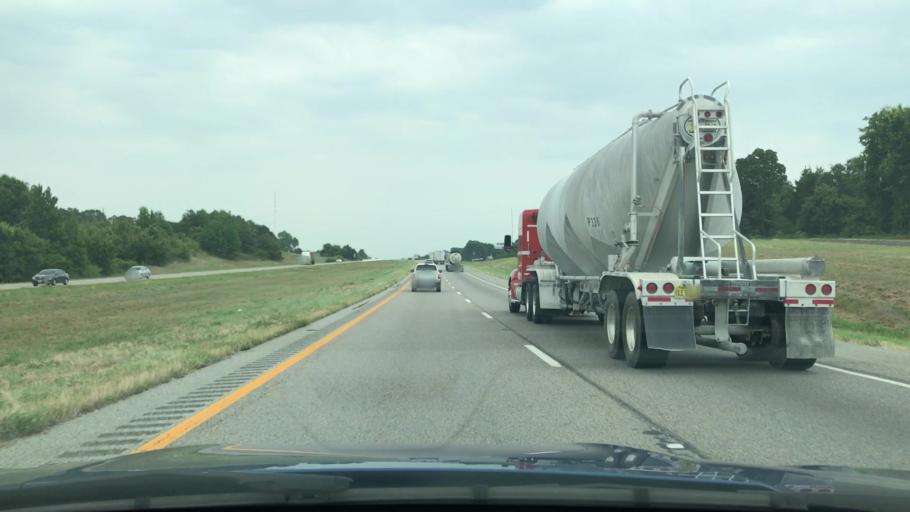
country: US
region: Texas
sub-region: Van Zandt County
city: Canton
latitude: 32.5484
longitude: -95.7734
